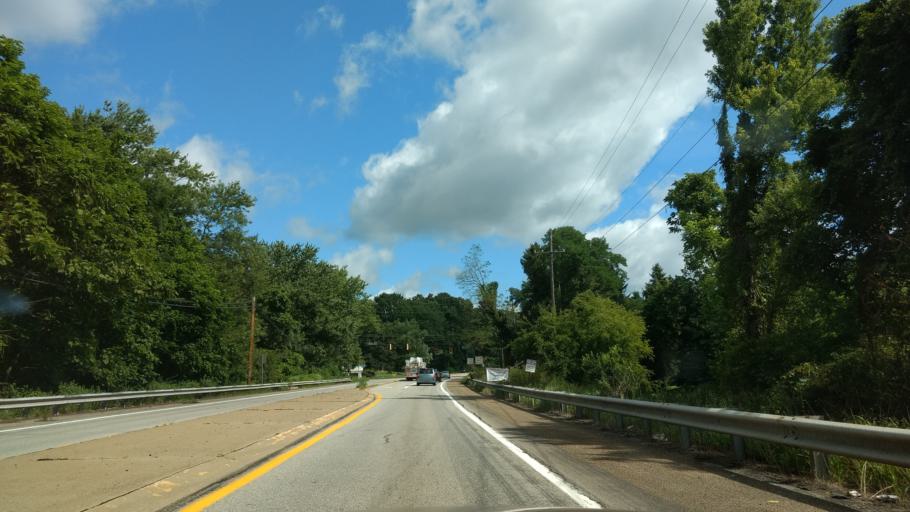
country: US
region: Pennsylvania
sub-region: Westmoreland County
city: Murrysville
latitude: 40.4741
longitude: -79.7073
